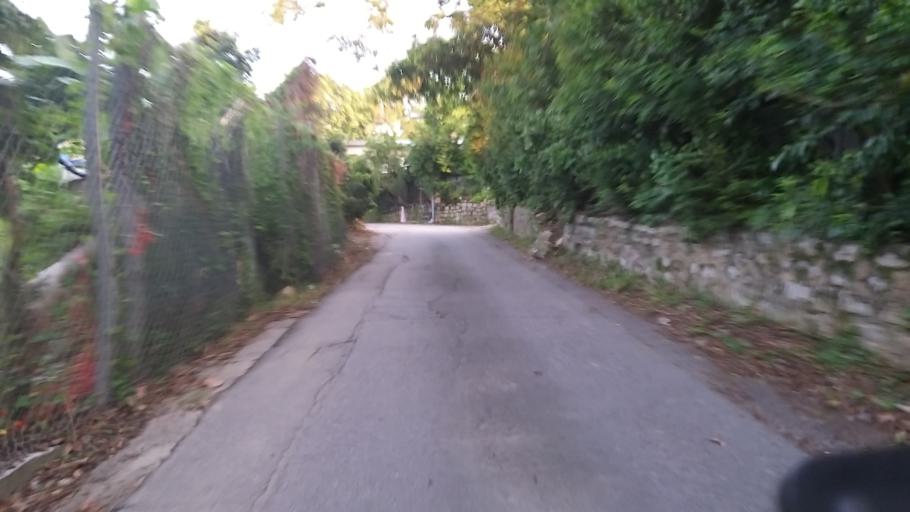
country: HK
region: Yuen Long
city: Yuen Long Kau Hui
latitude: 22.4486
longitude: 114.0146
